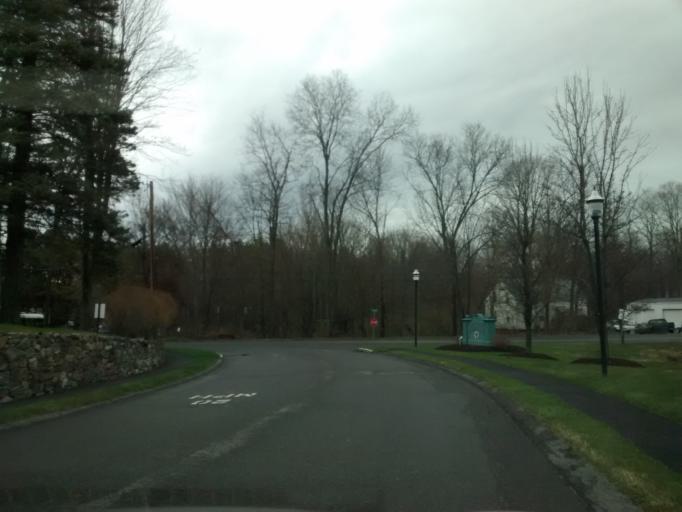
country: US
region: Massachusetts
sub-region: Worcester County
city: Shrewsbury
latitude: 42.2477
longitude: -71.7143
